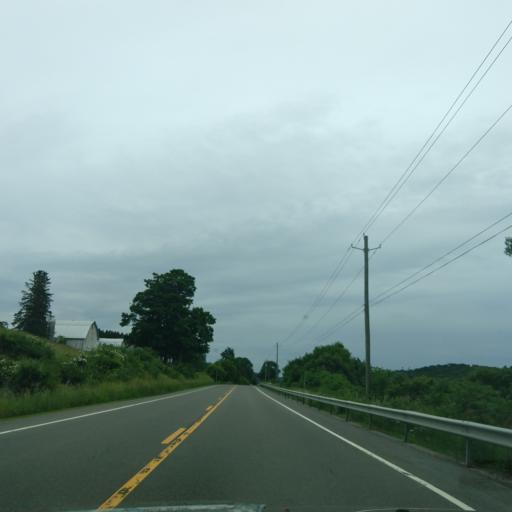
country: US
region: New York
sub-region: Cortland County
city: McGraw
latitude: 42.4797
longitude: -76.0620
